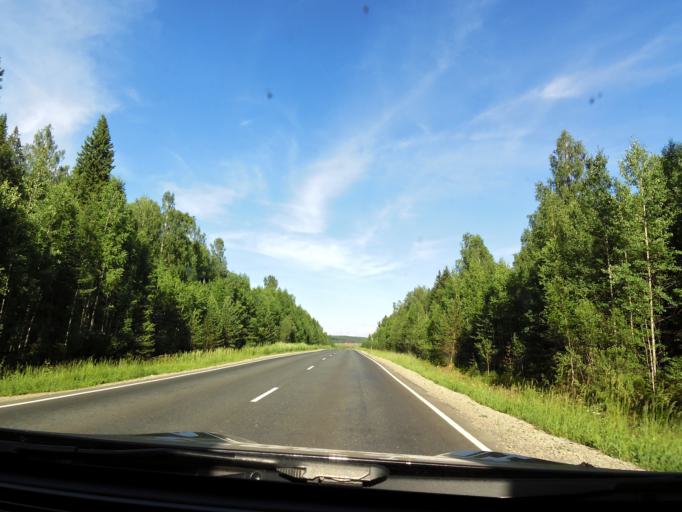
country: RU
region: Kirov
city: Chernaya Kholunitsa
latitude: 58.8589
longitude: 51.6726
